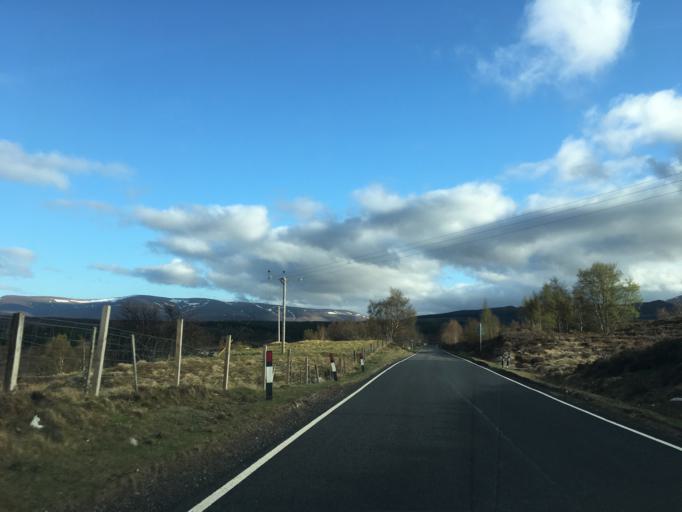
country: GB
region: Scotland
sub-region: Highland
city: Kingussie
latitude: 56.9967
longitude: -4.2484
